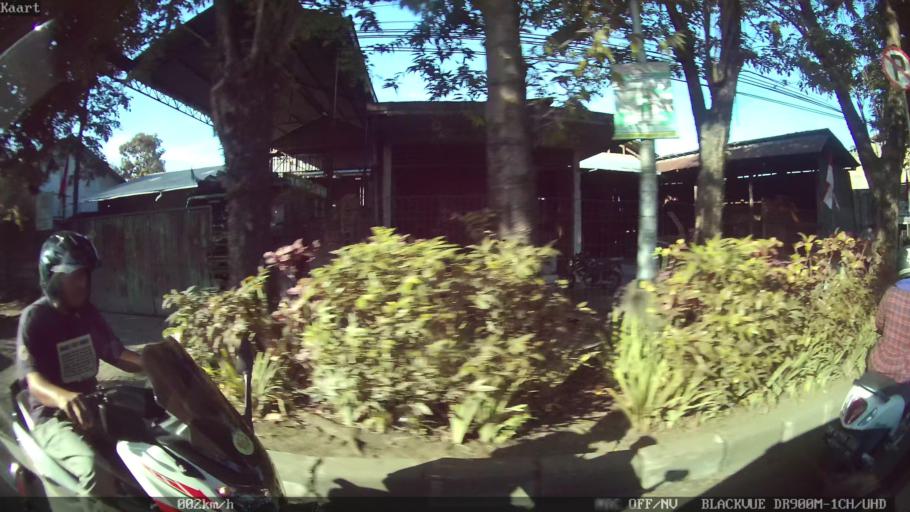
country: ID
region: Bali
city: Banjar Kertasari
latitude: -8.6167
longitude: 115.1946
